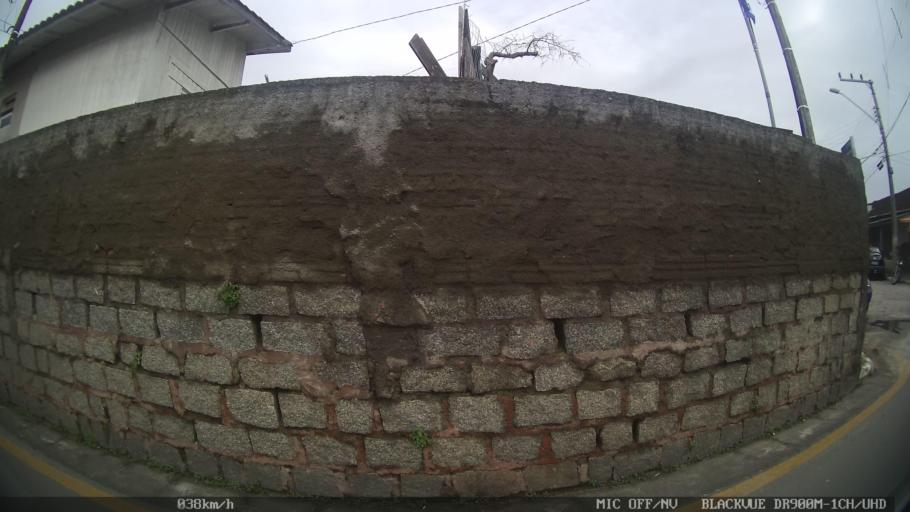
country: BR
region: Santa Catarina
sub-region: Sao Jose
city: Campinas
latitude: -27.5531
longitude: -48.6239
